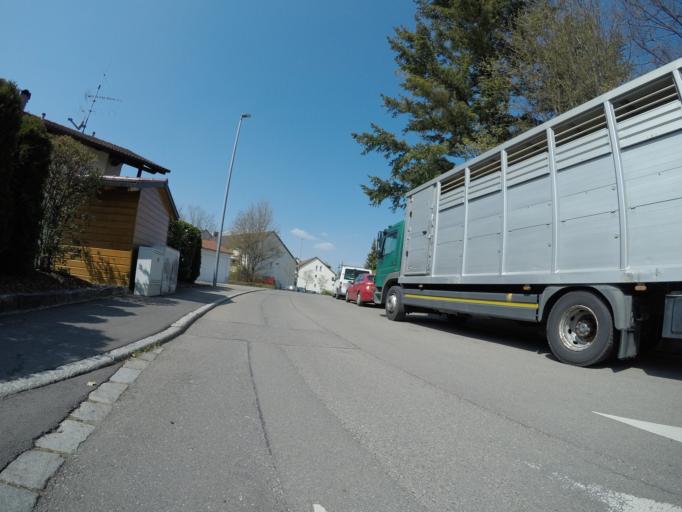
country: DE
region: Baden-Wuerttemberg
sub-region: Tuebingen Region
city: Wannweil
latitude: 48.4732
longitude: 9.1446
